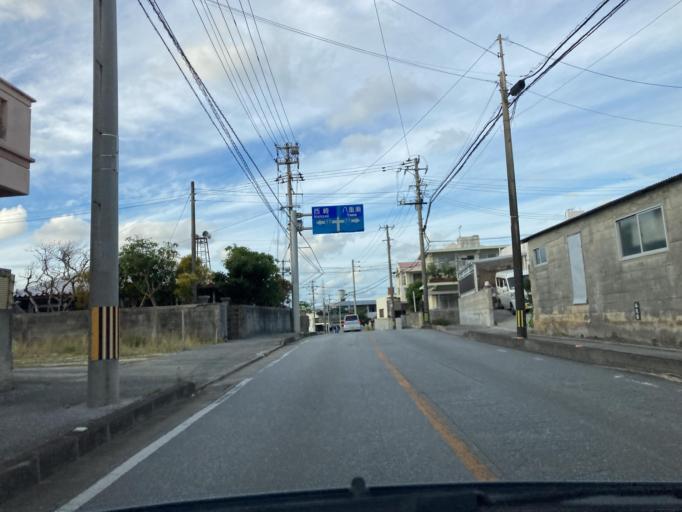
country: JP
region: Okinawa
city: Itoman
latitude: 26.1361
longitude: 127.6986
